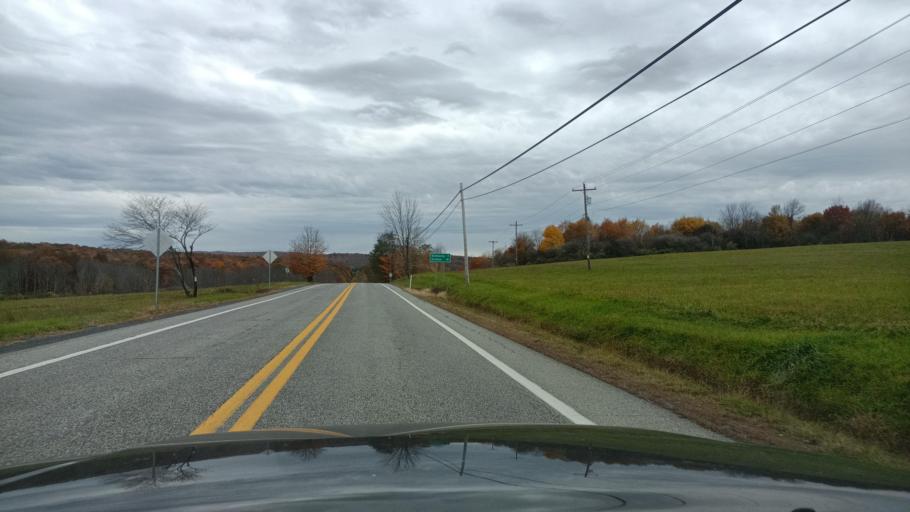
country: US
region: Maryland
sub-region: Garrett County
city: Mountain Lake Park
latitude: 39.2763
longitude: -79.2437
